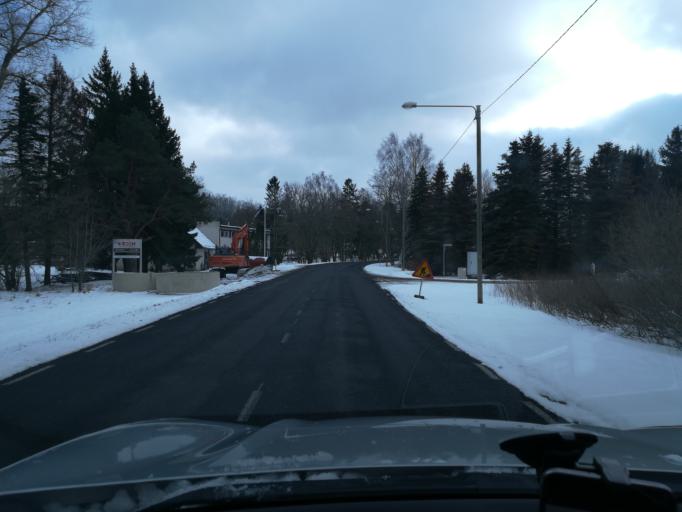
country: EE
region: Harju
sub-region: Keila linn
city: Keila
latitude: 59.3923
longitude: 24.4128
